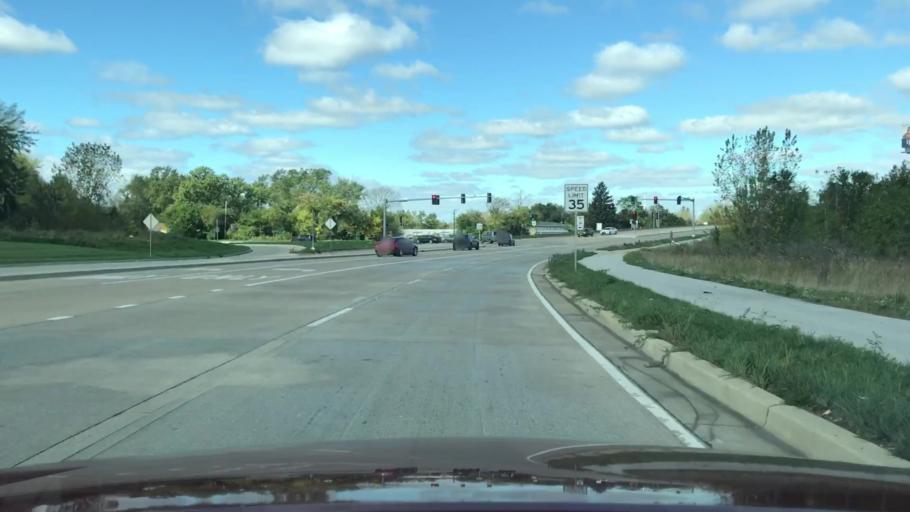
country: US
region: Indiana
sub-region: Lake County
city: Dyer
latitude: 41.4951
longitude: -87.5268
